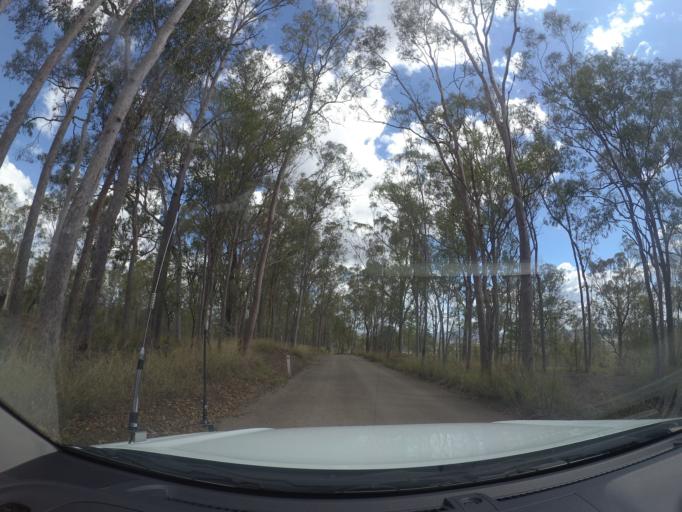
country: AU
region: Queensland
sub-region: Logan
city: Cedar Vale
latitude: -27.9001
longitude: 152.9871
